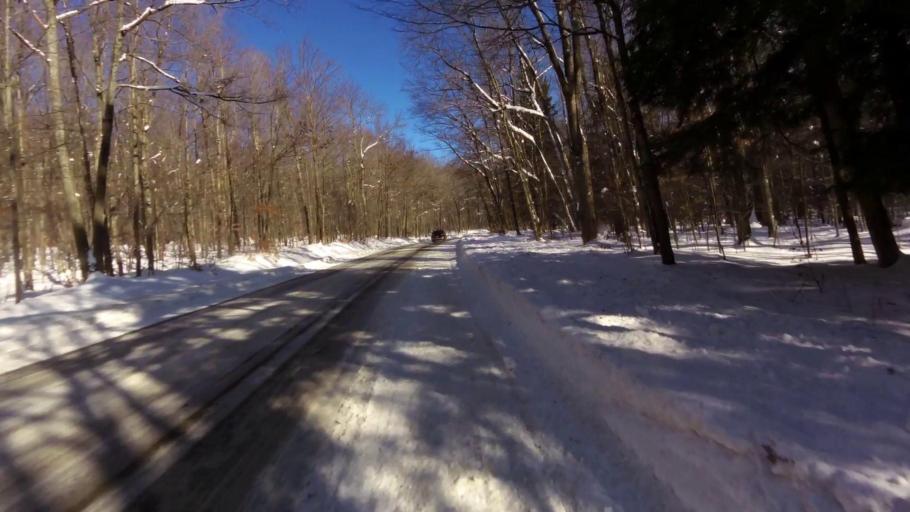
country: US
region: New York
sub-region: Cattaraugus County
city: Salamanca
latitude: 42.1231
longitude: -78.7286
